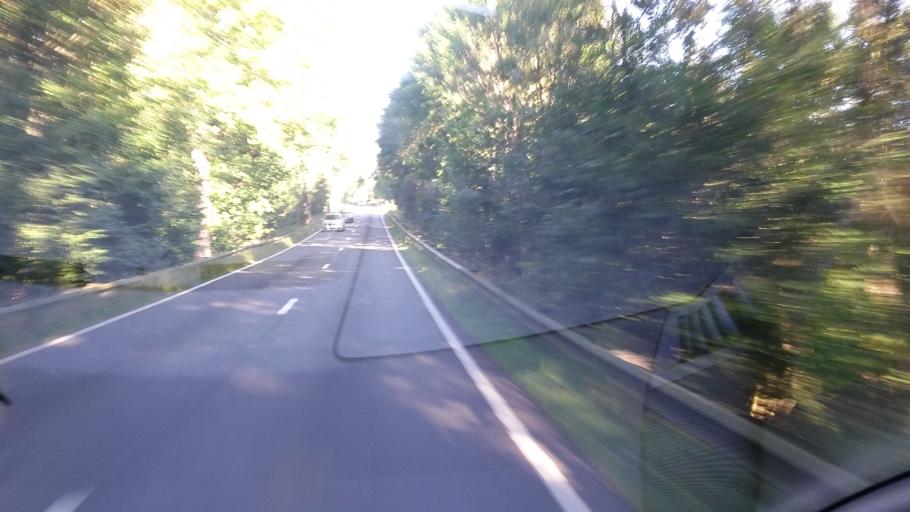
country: BE
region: Wallonia
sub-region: Province du Luxembourg
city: Leglise
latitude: 49.8115
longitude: 5.5064
